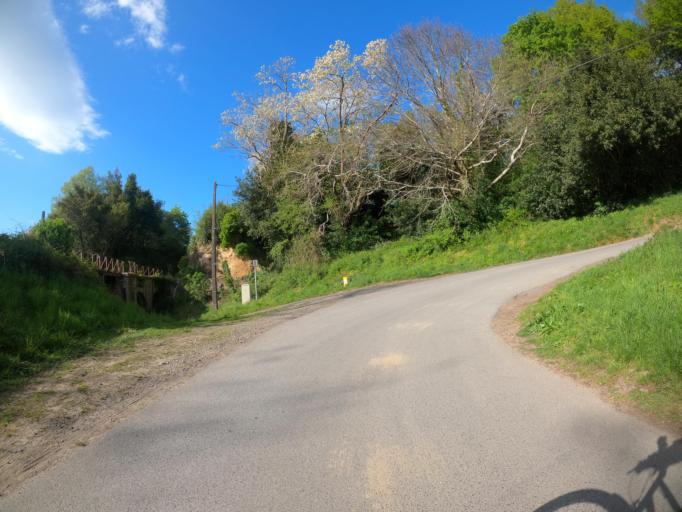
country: FR
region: Aquitaine
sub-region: Departement des Pyrenees-Atlantiques
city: Bayonne
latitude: 43.4780
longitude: -1.4686
